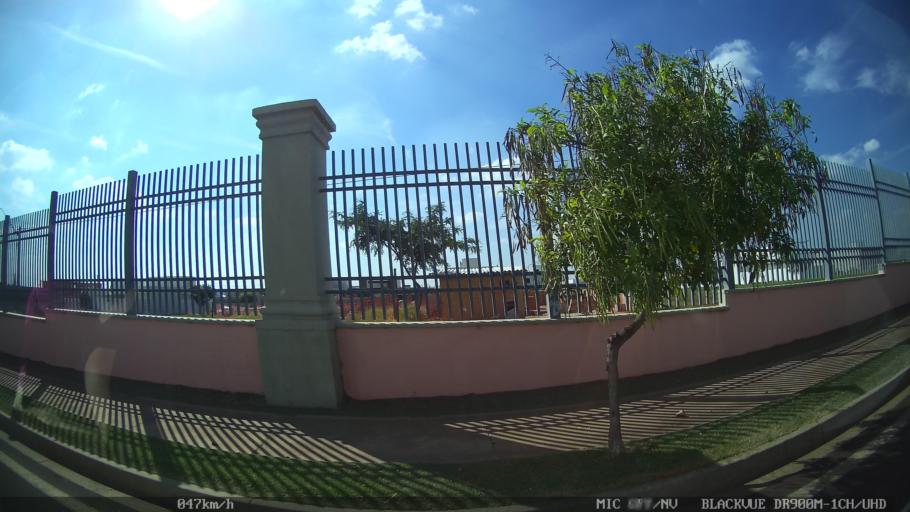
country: BR
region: Sao Paulo
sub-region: Hortolandia
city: Hortolandia
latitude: -22.8698
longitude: -47.2345
